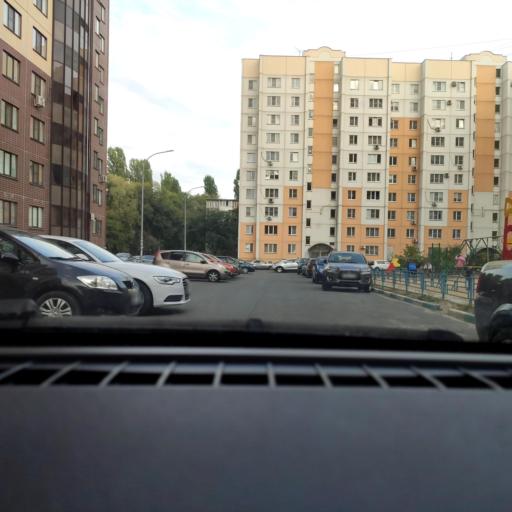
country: RU
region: Voronezj
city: Voronezh
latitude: 51.6492
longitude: 39.2345
